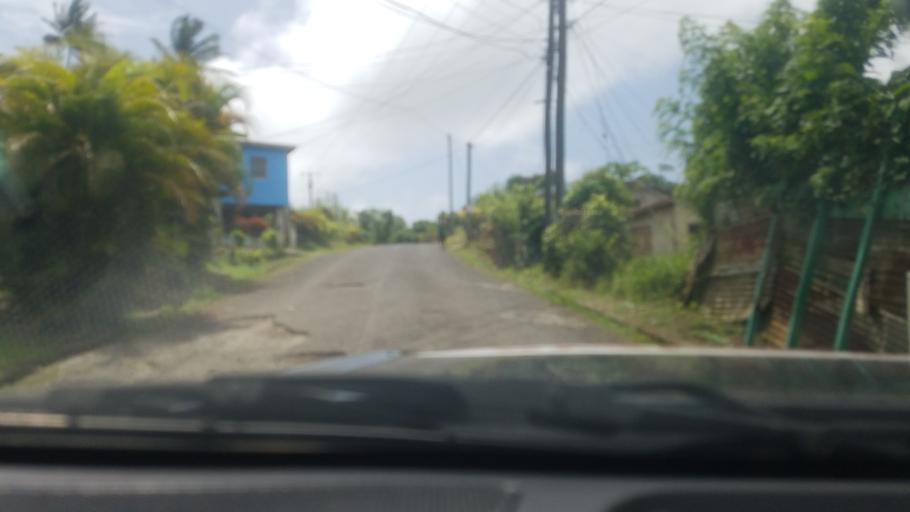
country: LC
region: Laborie Quarter
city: Laborie
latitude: 13.7909
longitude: -60.9534
